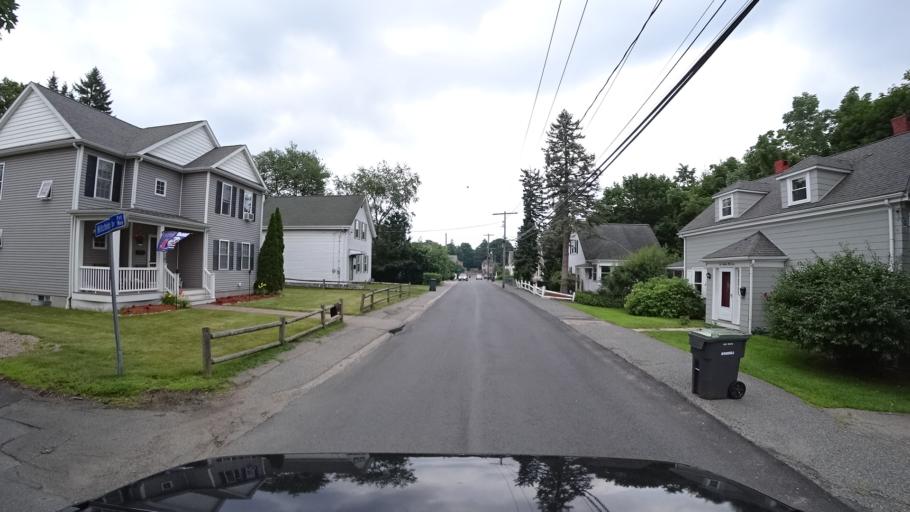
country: US
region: Massachusetts
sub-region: Norfolk County
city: Dedham
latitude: 42.2533
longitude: -71.1613
